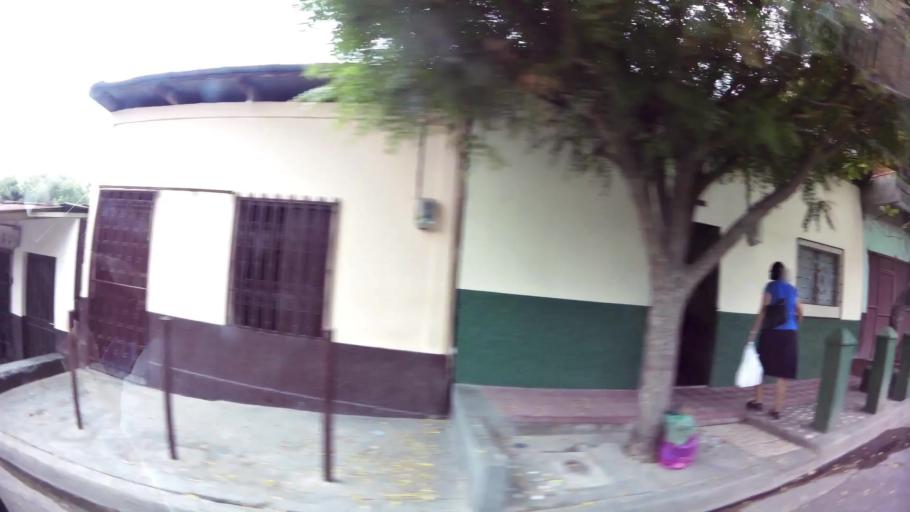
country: NI
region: Matagalpa
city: Matagalpa
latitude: 12.9232
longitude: -85.9159
